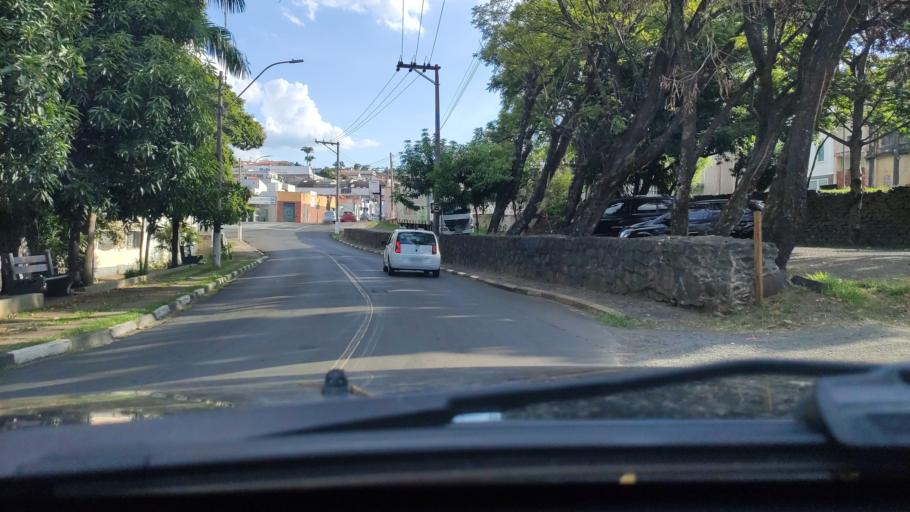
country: BR
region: Sao Paulo
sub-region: Itapira
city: Itapira
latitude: -22.4382
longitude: -46.8262
